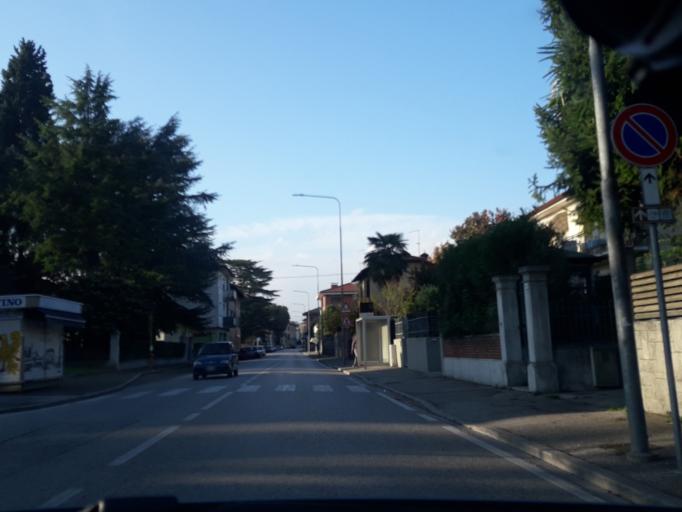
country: IT
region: Friuli Venezia Giulia
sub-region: Provincia di Udine
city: Udine
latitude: 46.0537
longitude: 13.2511
